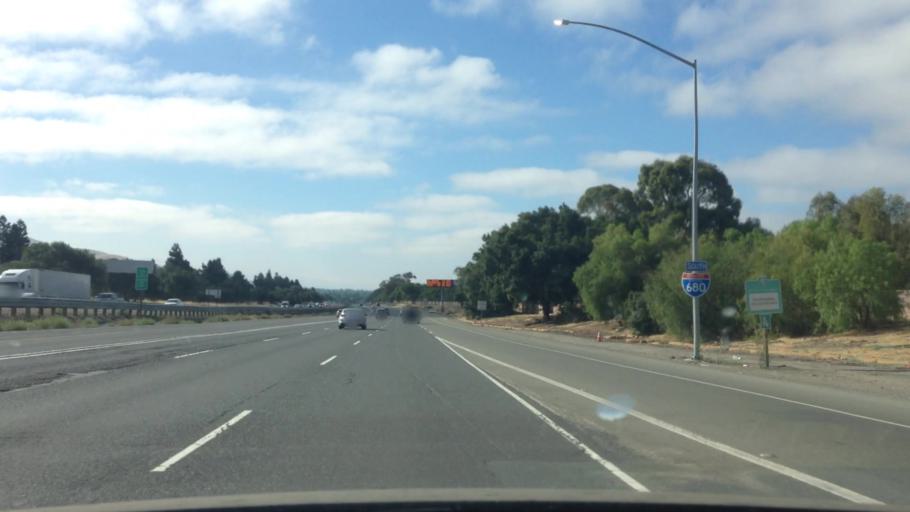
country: US
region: California
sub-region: Santa Clara County
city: Milpitas
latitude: 37.4637
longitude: -121.9037
